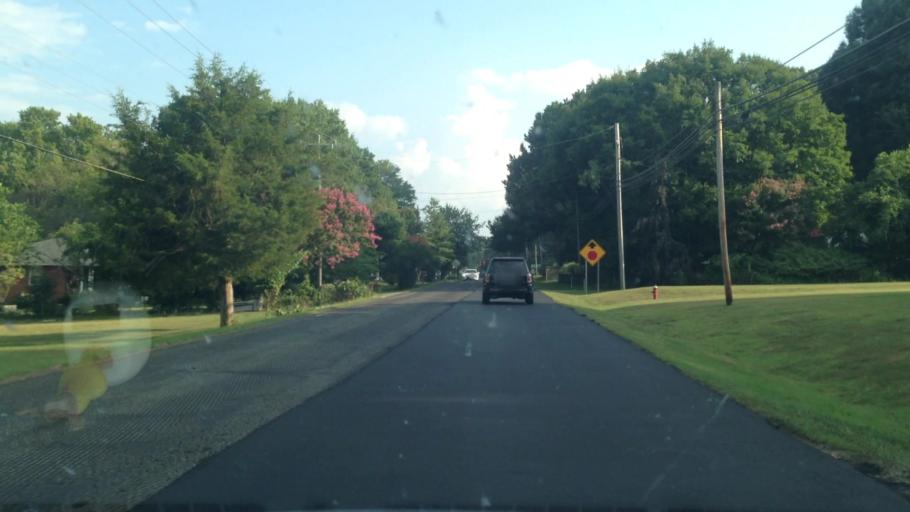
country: US
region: North Carolina
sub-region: Davidson County
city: Wallburg
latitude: 36.0222
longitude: -80.0594
